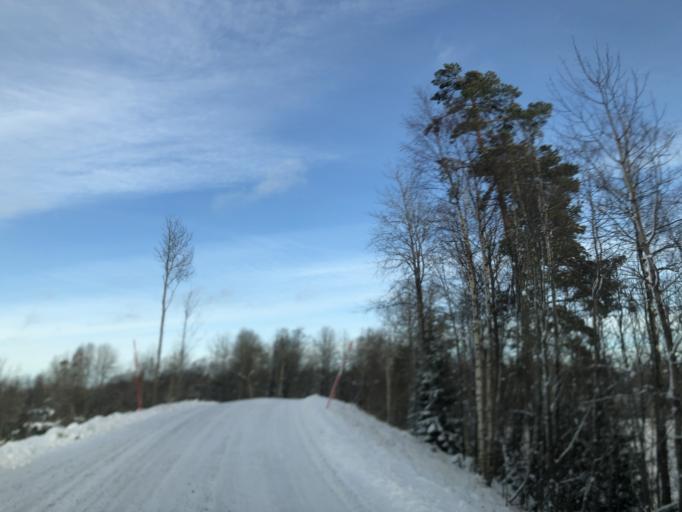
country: SE
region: Vaestra Goetaland
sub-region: Ulricehamns Kommun
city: Ulricehamn
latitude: 57.7699
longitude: 13.5217
